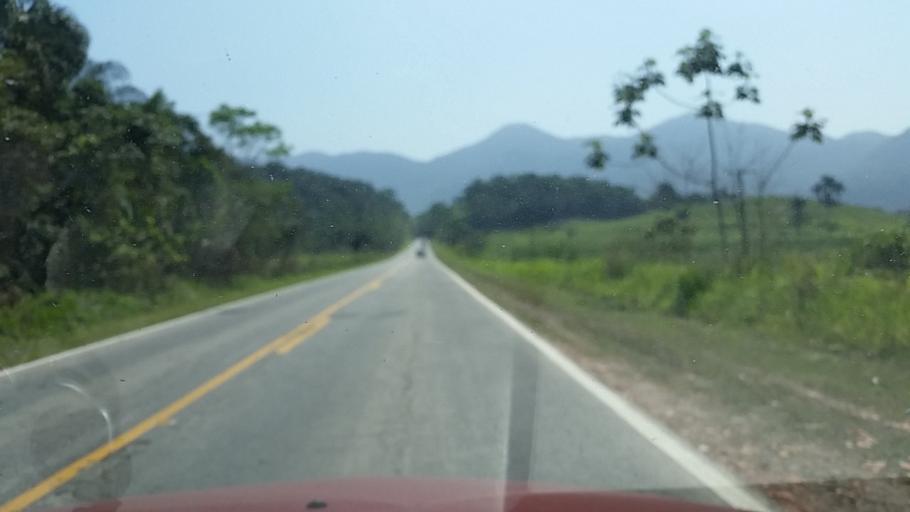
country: BR
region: Sao Paulo
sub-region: Juquia
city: Juquia
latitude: -24.3992
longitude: -47.5271
